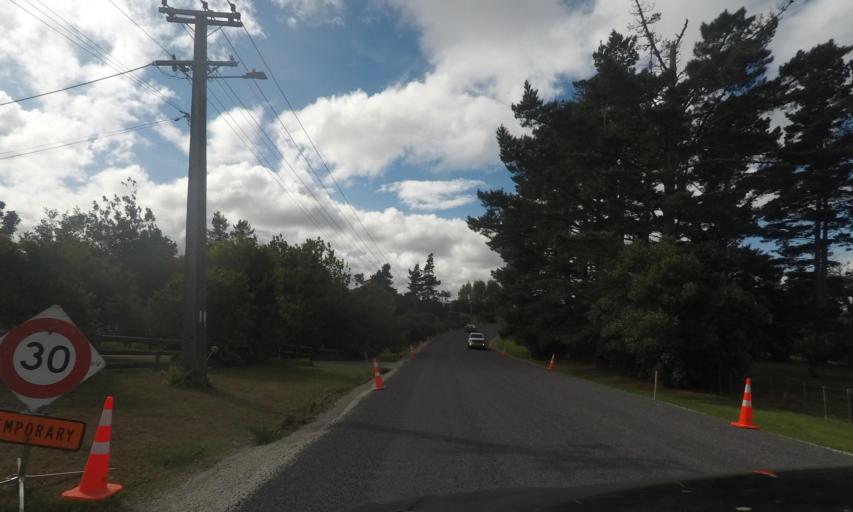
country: NZ
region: Auckland
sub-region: Auckland
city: Rosebank
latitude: -36.7909
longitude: 174.6370
